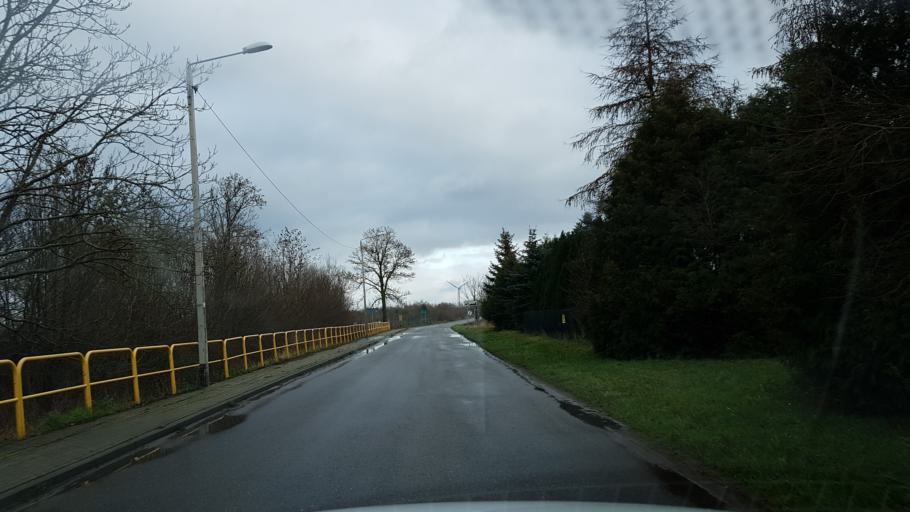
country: PL
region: West Pomeranian Voivodeship
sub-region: Powiat slawienski
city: Slawno
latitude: 54.5174
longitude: 16.6545
